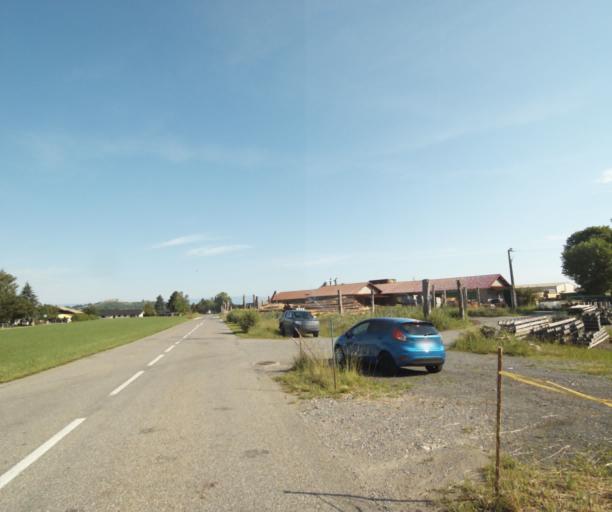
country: FR
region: Rhone-Alpes
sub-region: Departement de la Haute-Savoie
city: Allinges
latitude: 46.3128
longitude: 6.4861
